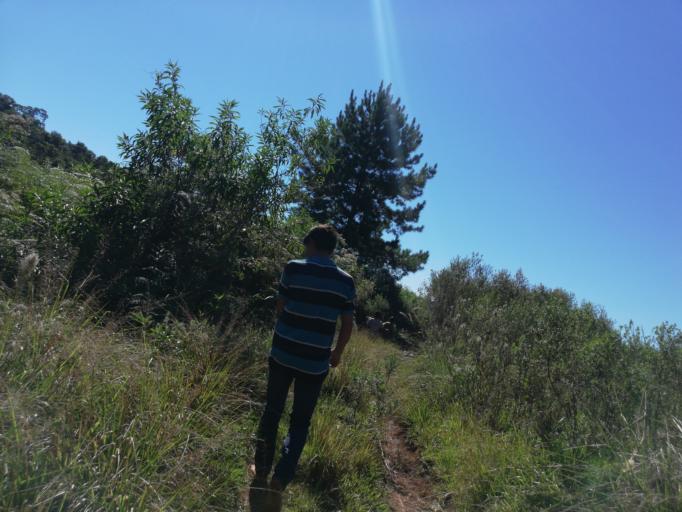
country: AR
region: Misiones
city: El Soberbio
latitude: -27.0628
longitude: -54.3773
